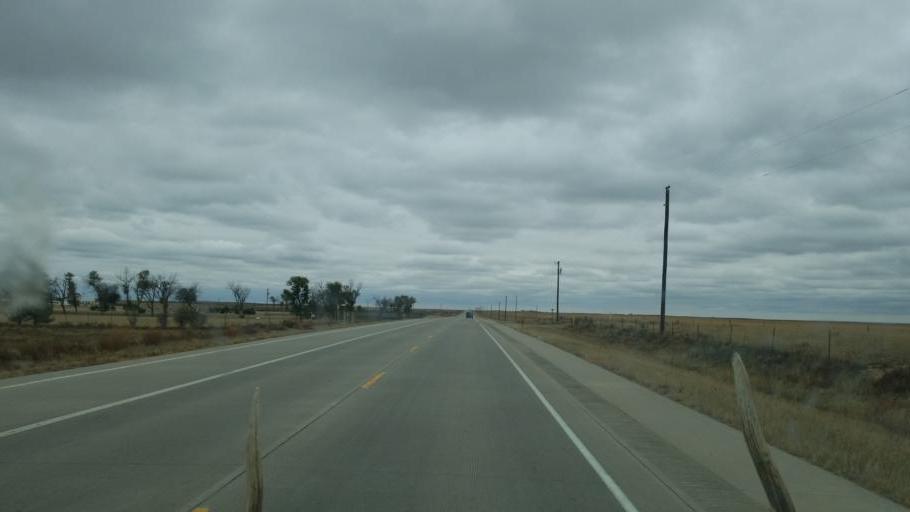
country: US
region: Colorado
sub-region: Kiowa County
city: Eads
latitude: 38.6572
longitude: -102.7859
